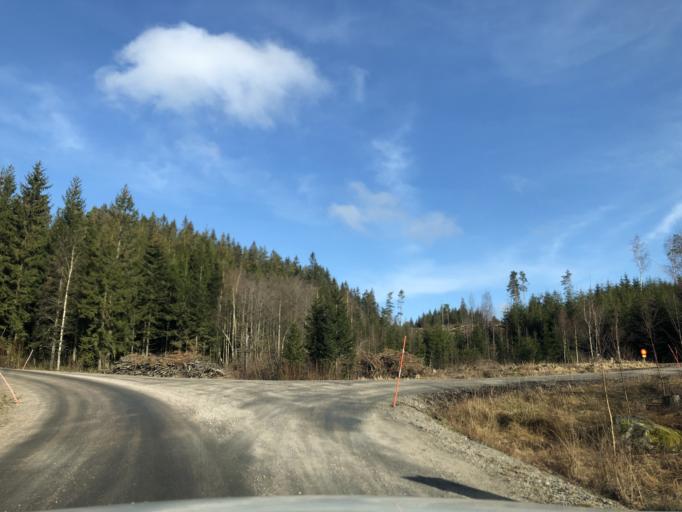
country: SE
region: Vaestra Goetaland
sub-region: Ulricehamns Kommun
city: Ulricehamn
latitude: 57.8125
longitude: 13.3805
